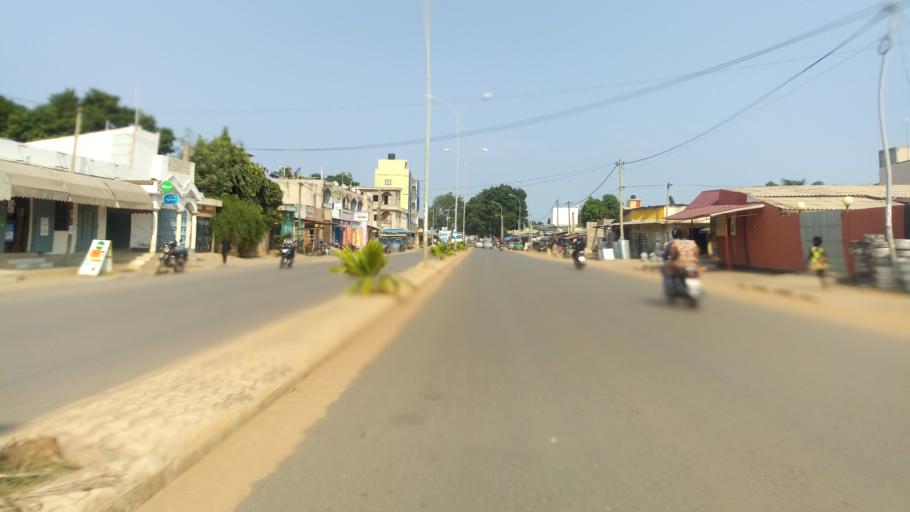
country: TG
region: Maritime
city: Lome
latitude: 6.1973
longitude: 1.1860
